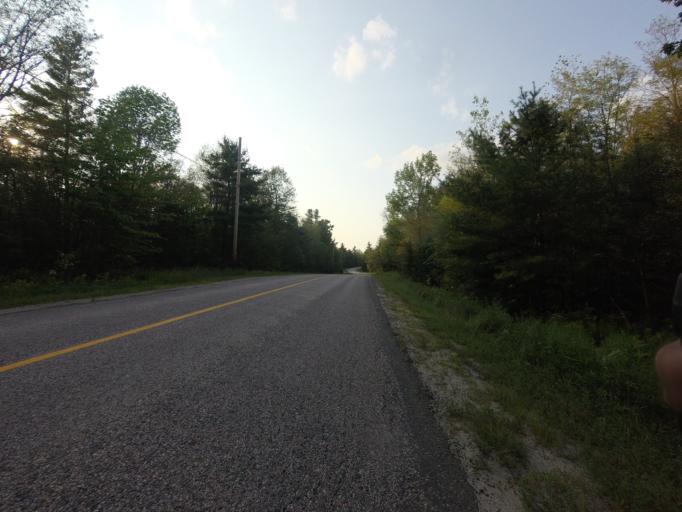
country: CA
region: Ontario
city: Renfrew
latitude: 44.9946
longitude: -76.7464
